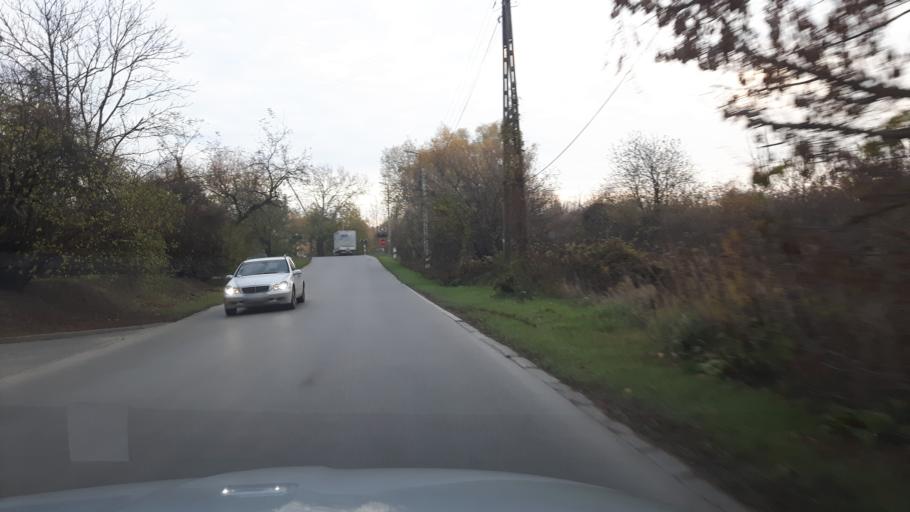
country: PL
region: Masovian Voivodeship
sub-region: Warszawa
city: Wilanow
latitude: 52.1825
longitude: 21.0985
